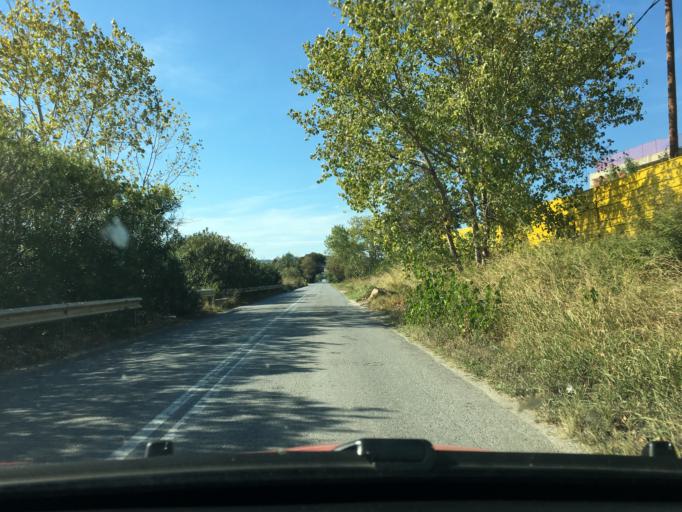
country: GR
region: Central Macedonia
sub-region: Nomos Chalkidikis
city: Nea Roda
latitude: 40.3607
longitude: 23.9328
